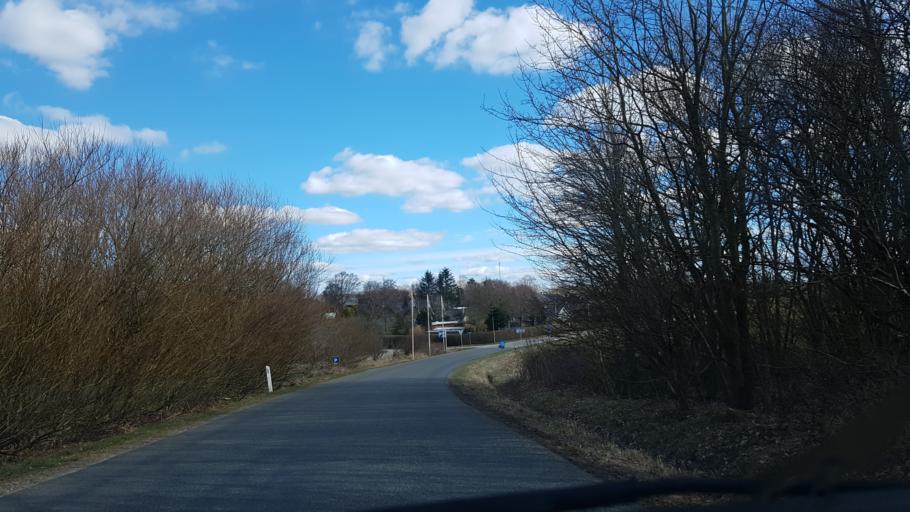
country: DK
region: South Denmark
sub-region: Vejen Kommune
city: Brorup
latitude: 55.4097
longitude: 8.9634
